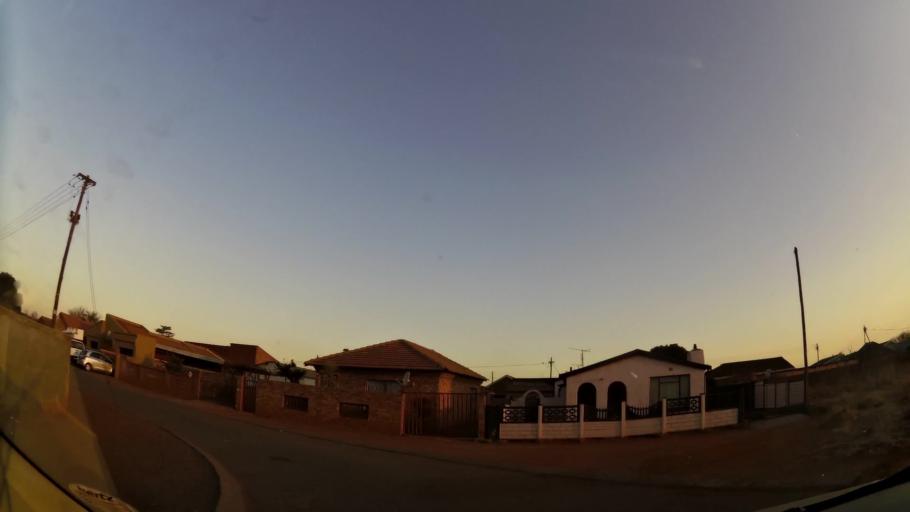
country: ZA
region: Gauteng
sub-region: West Rand District Municipality
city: Randfontein
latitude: -26.2012
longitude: 27.7095
